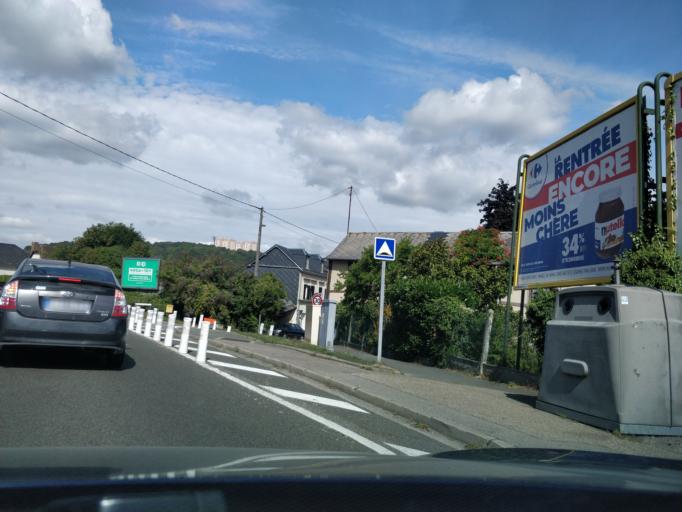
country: FR
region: Haute-Normandie
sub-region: Departement de la Seine-Maritime
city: Saint-Leger-du-Bourg-Denis
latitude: 49.4349
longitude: 1.1505
